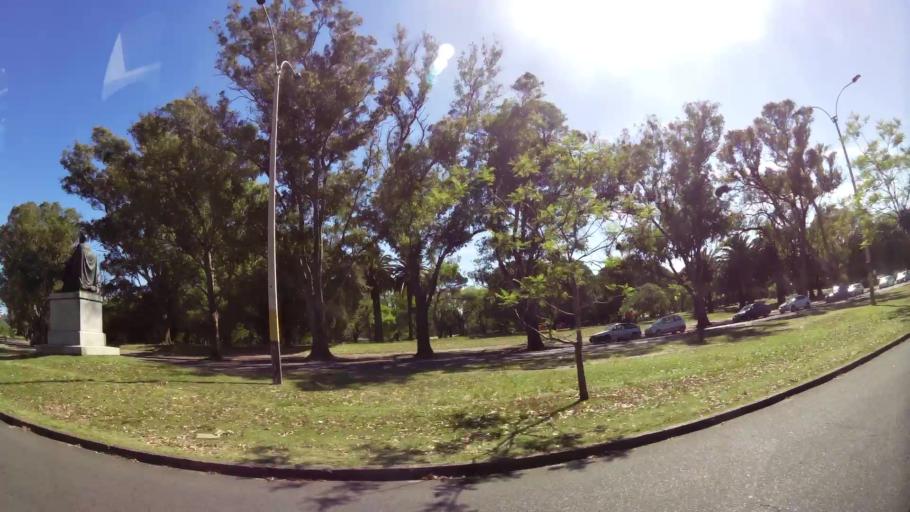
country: UY
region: Montevideo
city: Montevideo
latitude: -34.8975
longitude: -56.1588
